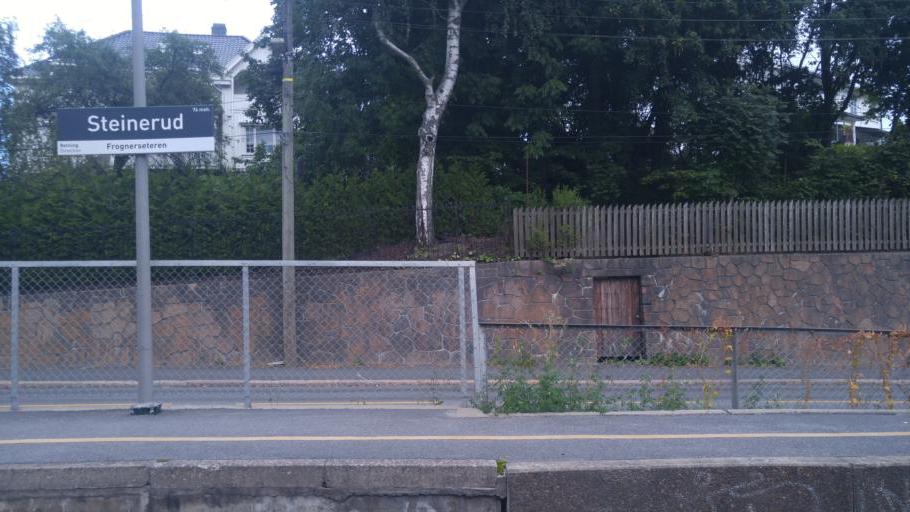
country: NO
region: Oslo
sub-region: Oslo
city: Sjolyststranda
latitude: 59.9390
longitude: 10.7044
